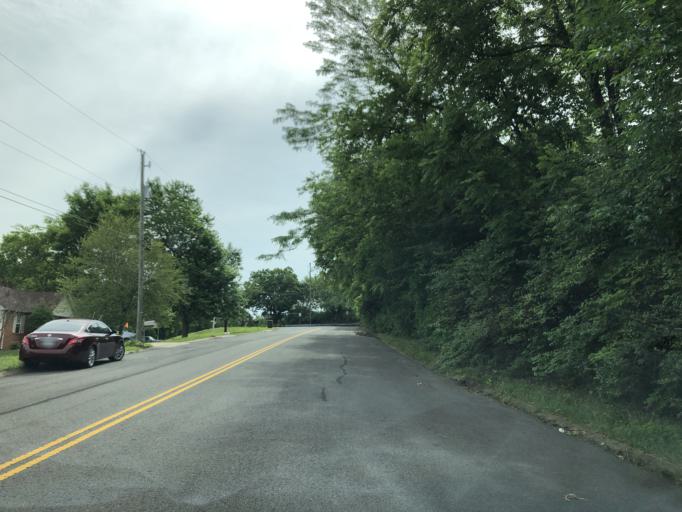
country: US
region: Tennessee
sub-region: Davidson County
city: Goodlettsville
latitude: 36.2825
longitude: -86.7109
